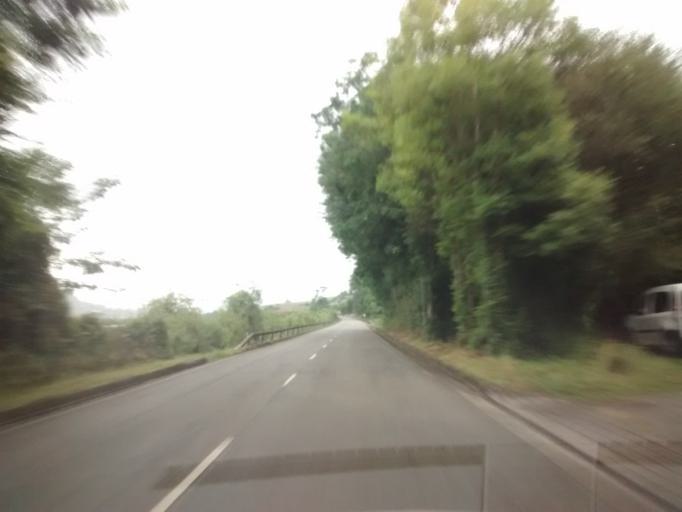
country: ES
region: Asturias
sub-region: Province of Asturias
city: Villaviciosa
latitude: 43.5068
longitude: -5.4225
